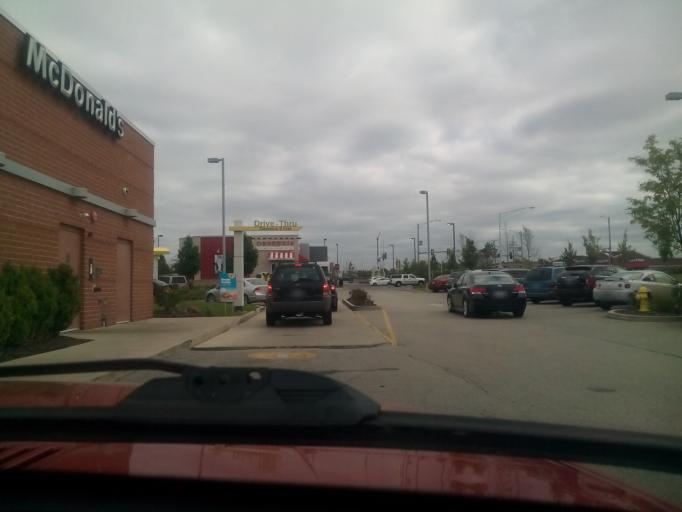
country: US
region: Illinois
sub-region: DuPage County
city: Woodridge
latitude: 41.7266
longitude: -88.0323
